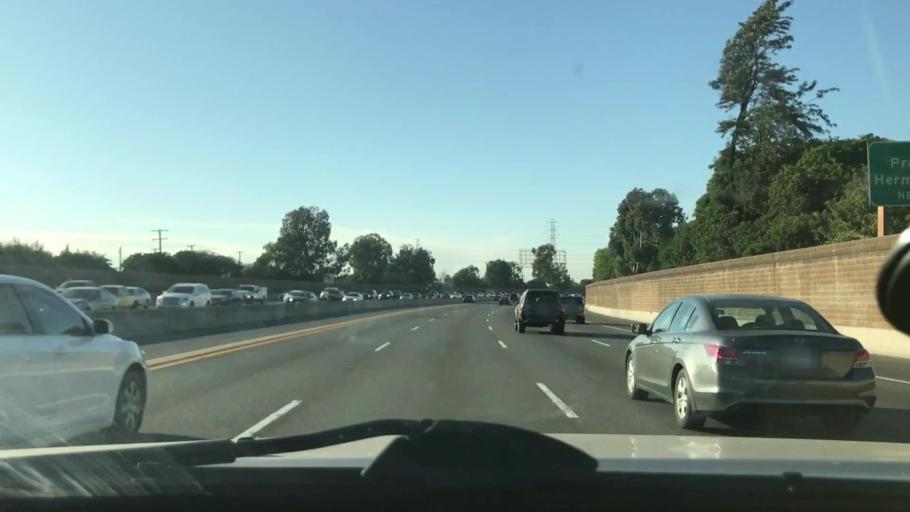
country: US
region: California
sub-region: Los Angeles County
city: Alondra Park
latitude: 33.8675
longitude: -118.3352
